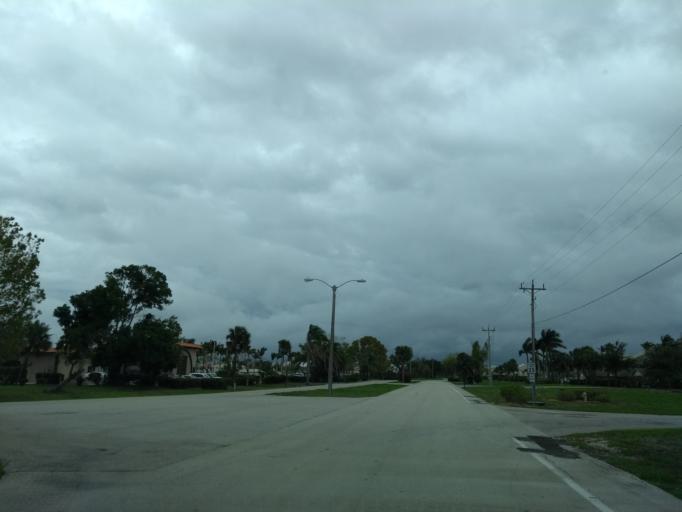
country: US
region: Florida
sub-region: Collier County
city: Marco
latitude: 25.9581
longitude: -81.5123
